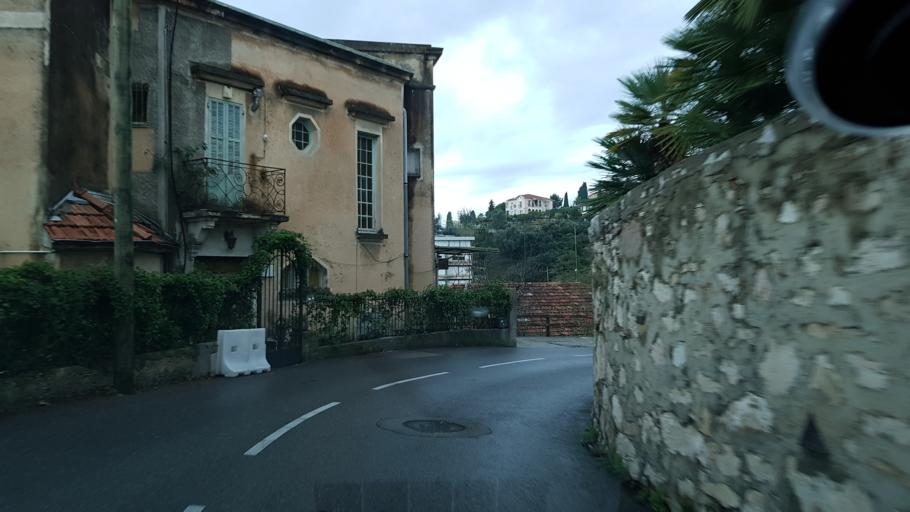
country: FR
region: Provence-Alpes-Cote d'Azur
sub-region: Departement des Alpes-Maritimes
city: Nice
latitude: 43.6950
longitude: 7.2393
